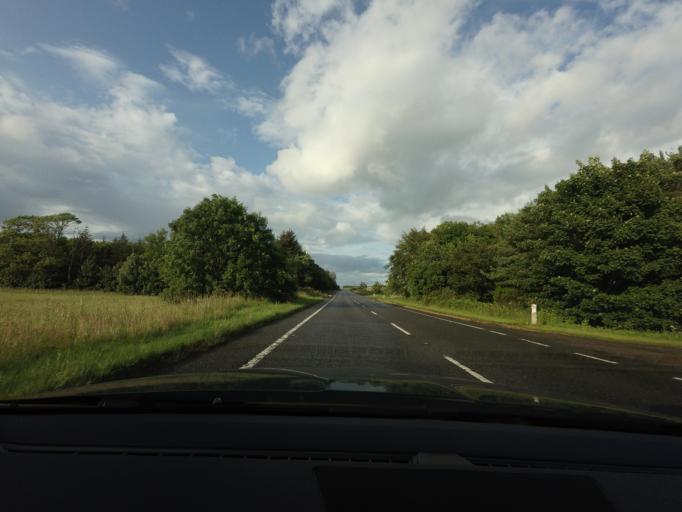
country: GB
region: Scotland
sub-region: Highland
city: Fortrose
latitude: 57.5382
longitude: -4.0212
